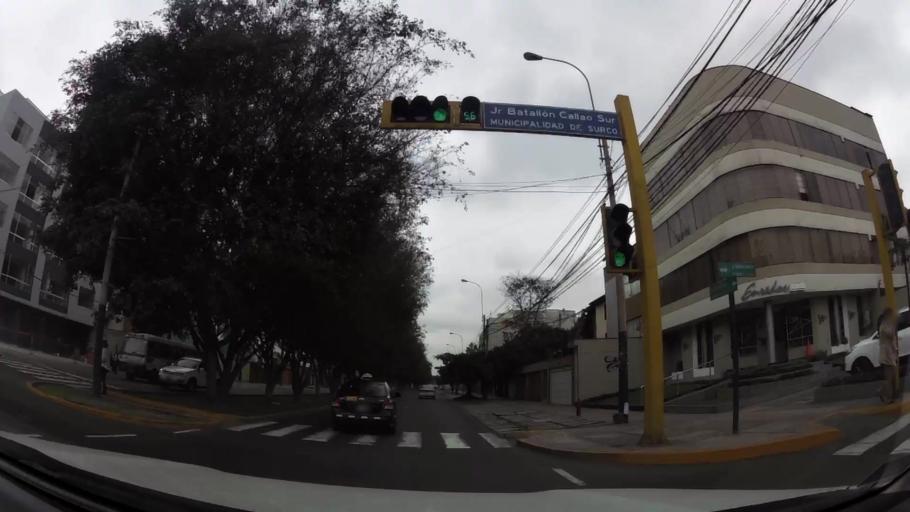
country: PE
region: Lima
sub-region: Lima
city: Surco
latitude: -12.1250
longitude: -76.9833
